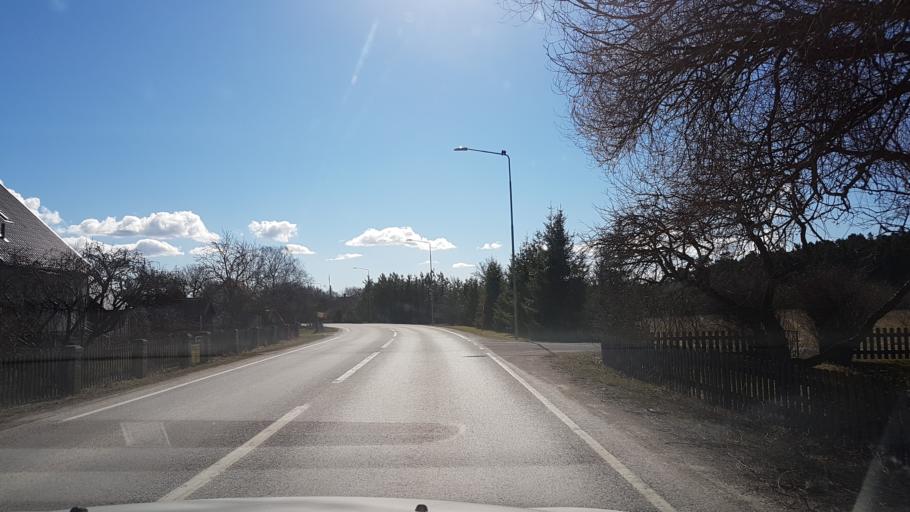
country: SE
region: Gotland
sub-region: Gotland
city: Visby
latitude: 57.5191
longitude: 18.4431
